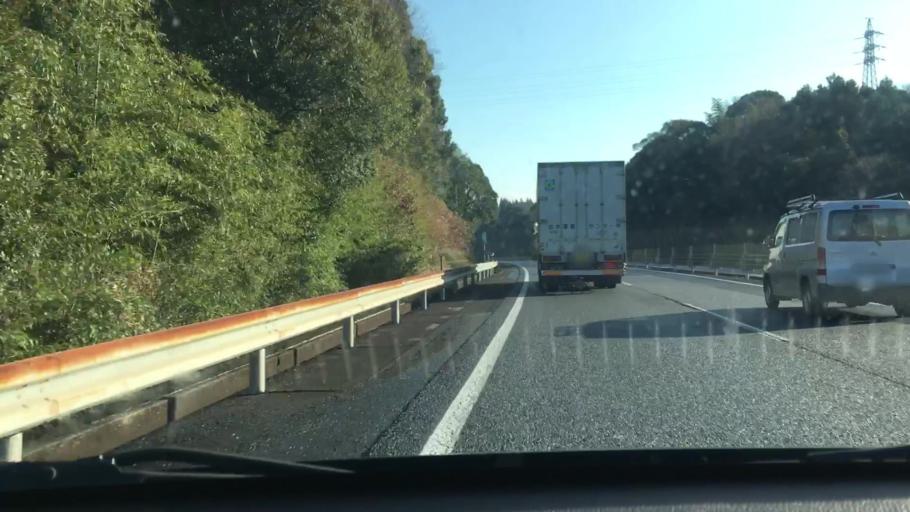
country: JP
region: Kagoshima
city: Okuchi-shinohara
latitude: 31.9156
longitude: 130.7032
